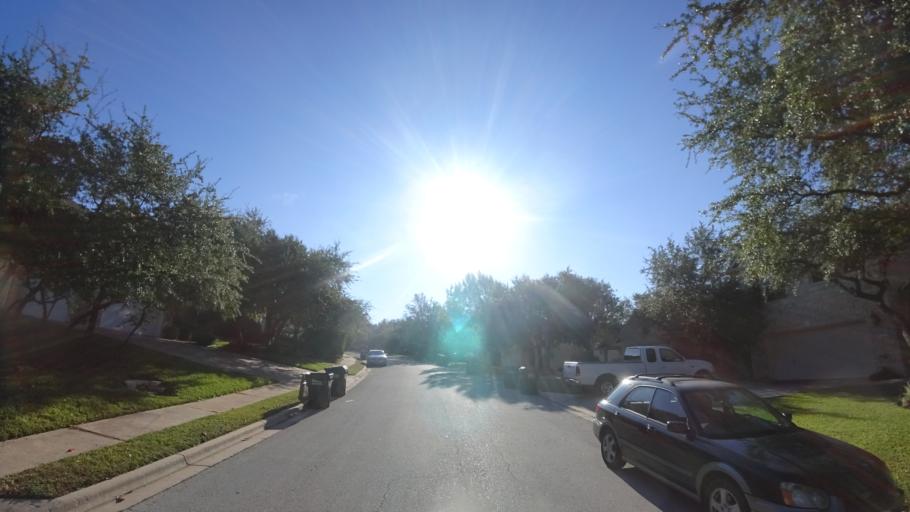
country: US
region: Texas
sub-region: Travis County
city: Hudson Bend
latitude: 30.3692
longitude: -97.9000
